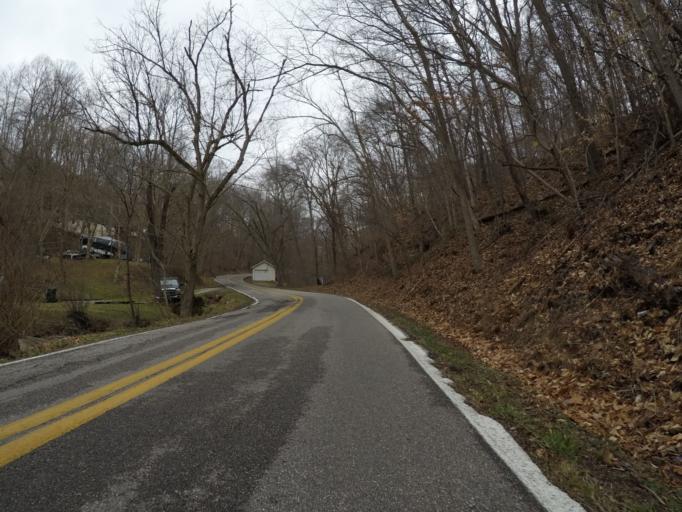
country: US
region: West Virginia
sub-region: Cabell County
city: Barboursville
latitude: 38.4536
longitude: -82.2633
